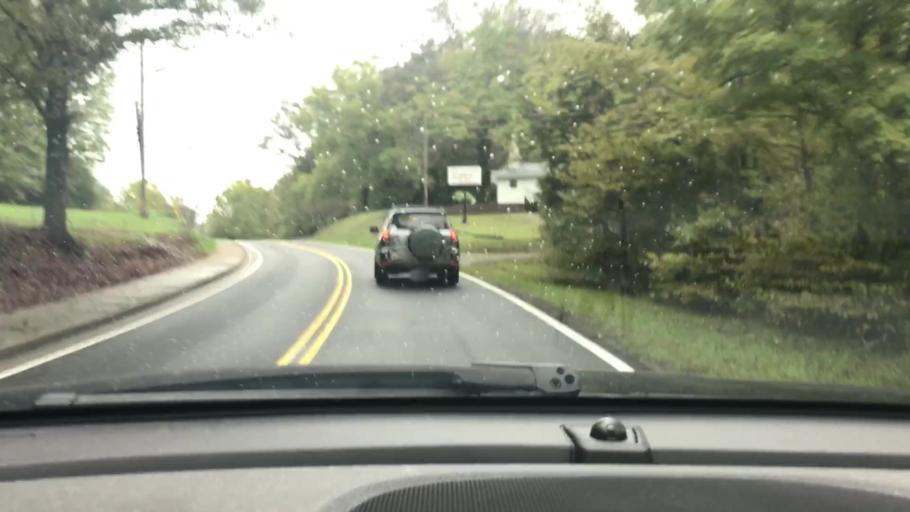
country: US
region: Tennessee
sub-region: Cheatham County
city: Kingston Springs
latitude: 36.0940
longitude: -87.1106
